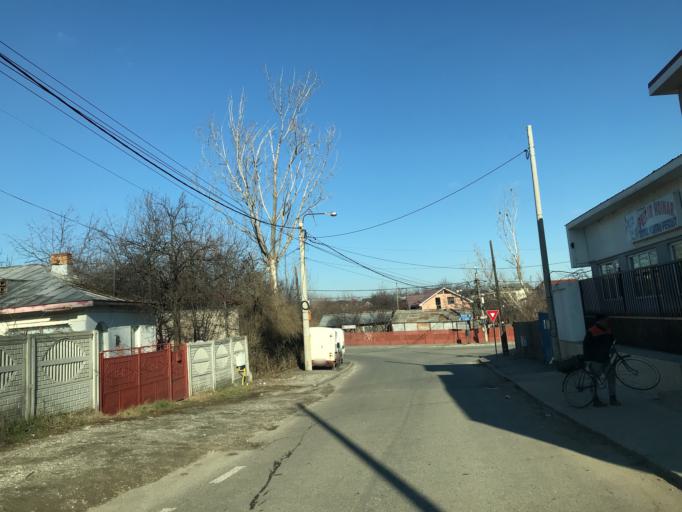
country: RO
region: Olt
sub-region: Municipiul Slatina
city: Slatina
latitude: 44.4175
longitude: 24.3635
